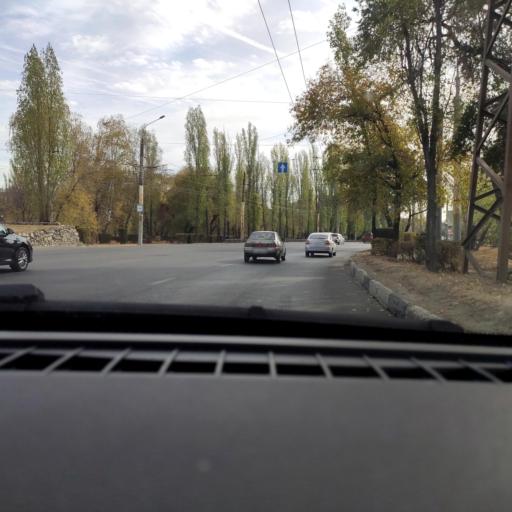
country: RU
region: Voronezj
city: Voronezh
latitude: 51.6319
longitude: 39.2278
